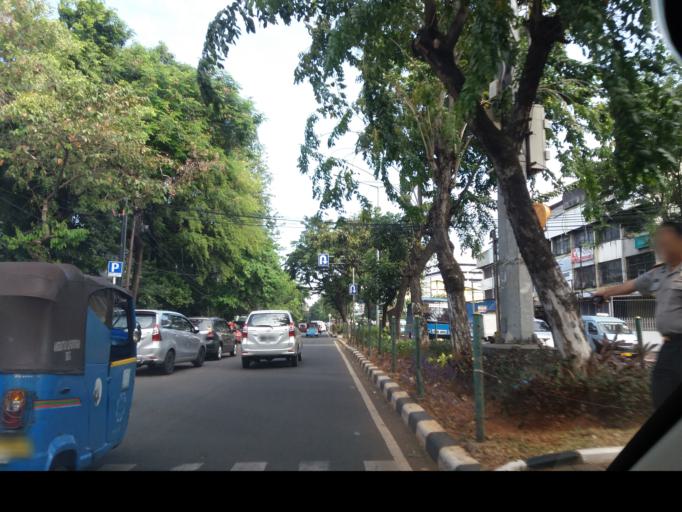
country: ID
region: Jakarta Raya
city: Jakarta
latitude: -6.1723
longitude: 106.8430
